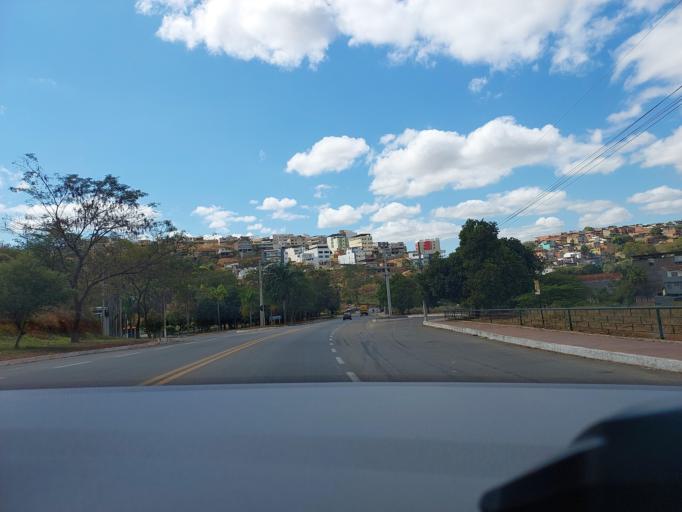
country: BR
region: Minas Gerais
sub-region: Muriae
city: Muriae
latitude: -21.1263
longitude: -42.3565
